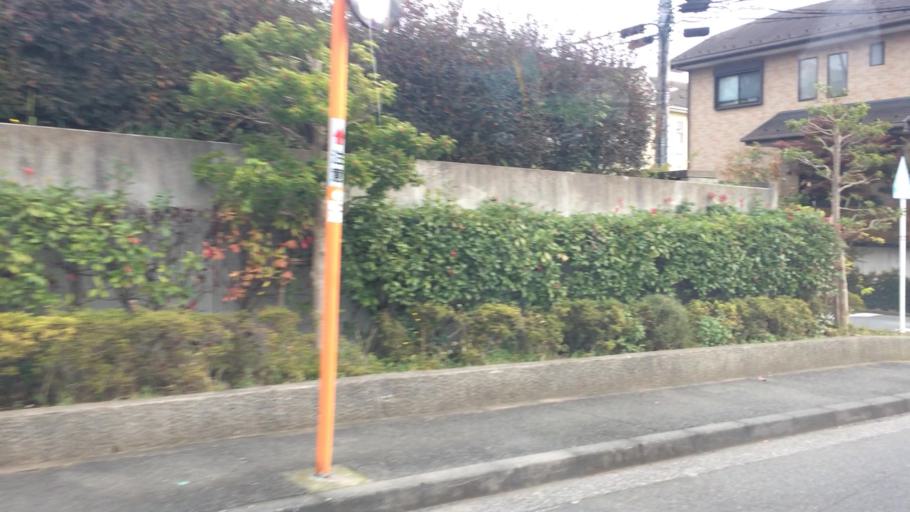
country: JP
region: Tokyo
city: Chofugaoka
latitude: 35.5613
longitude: 139.6004
